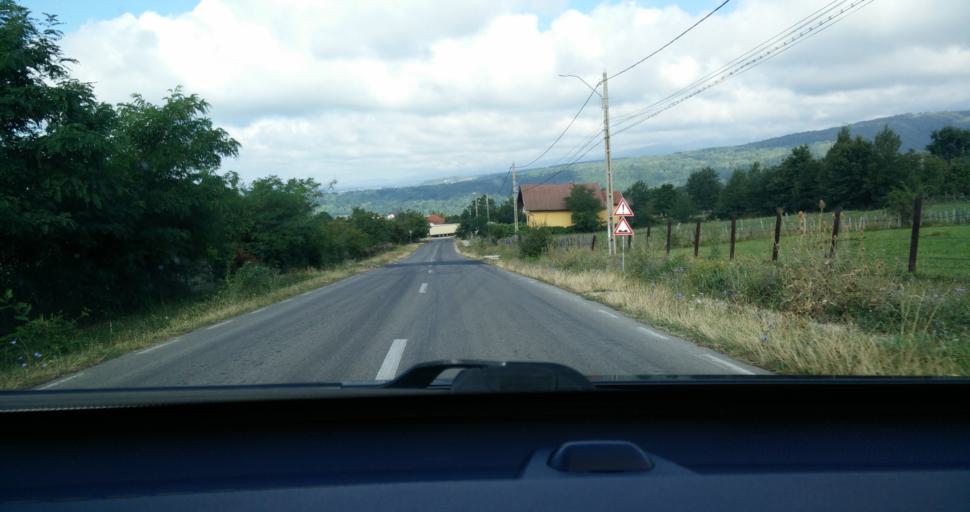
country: RO
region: Gorj
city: Novaci-Straini
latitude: 45.1801
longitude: 23.6913
